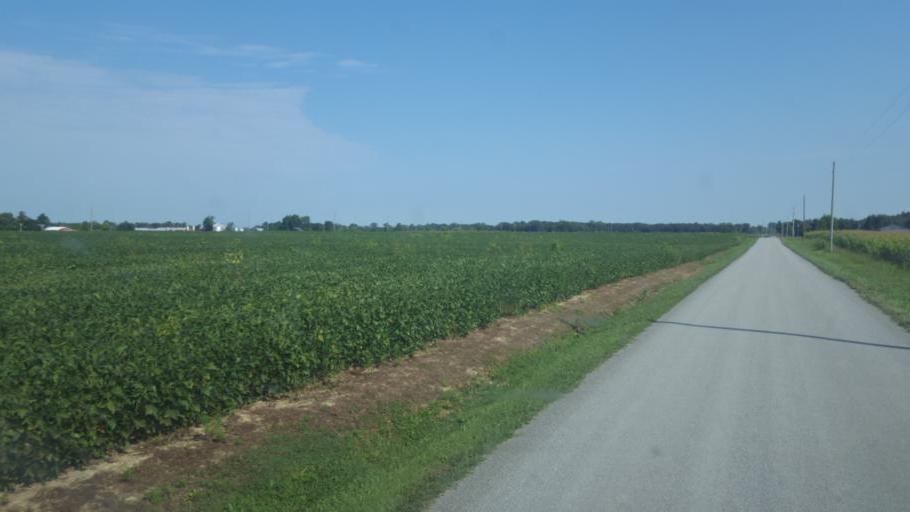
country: US
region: Ohio
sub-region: Morrow County
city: Cardington
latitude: 40.4796
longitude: -82.9489
